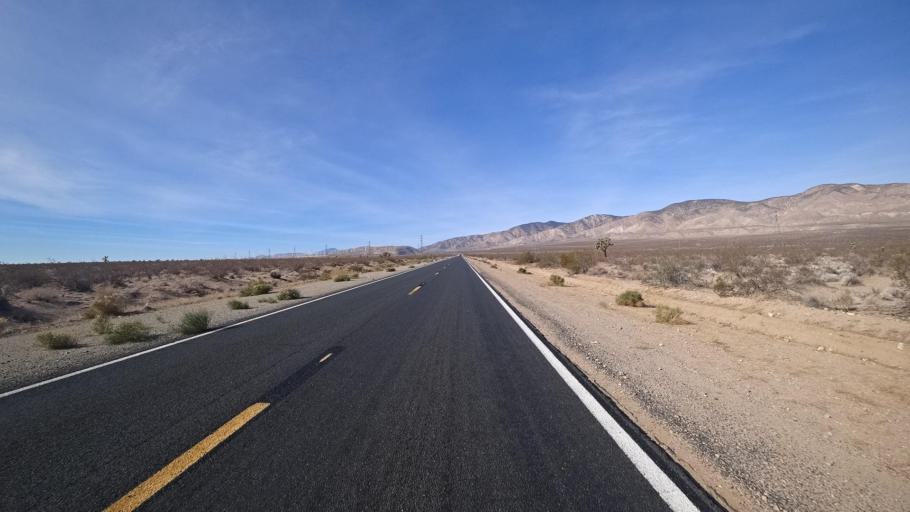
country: US
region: California
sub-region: Kern County
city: Mojave
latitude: 35.1252
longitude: -118.1504
